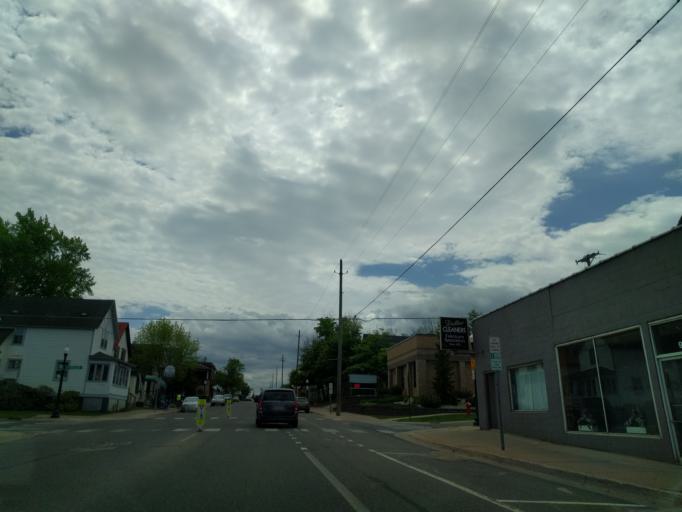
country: US
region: Michigan
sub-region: Marquette County
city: Marquette
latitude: 46.5515
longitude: -87.3948
